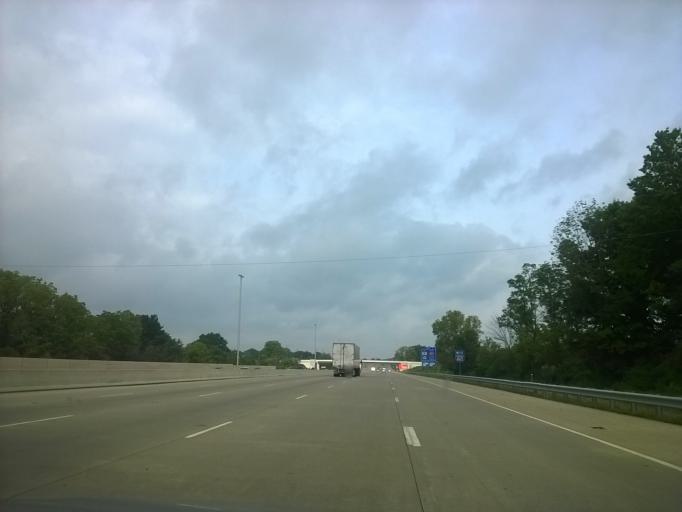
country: US
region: Indiana
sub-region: Marion County
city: Meridian Hills
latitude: 39.9244
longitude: -86.1220
